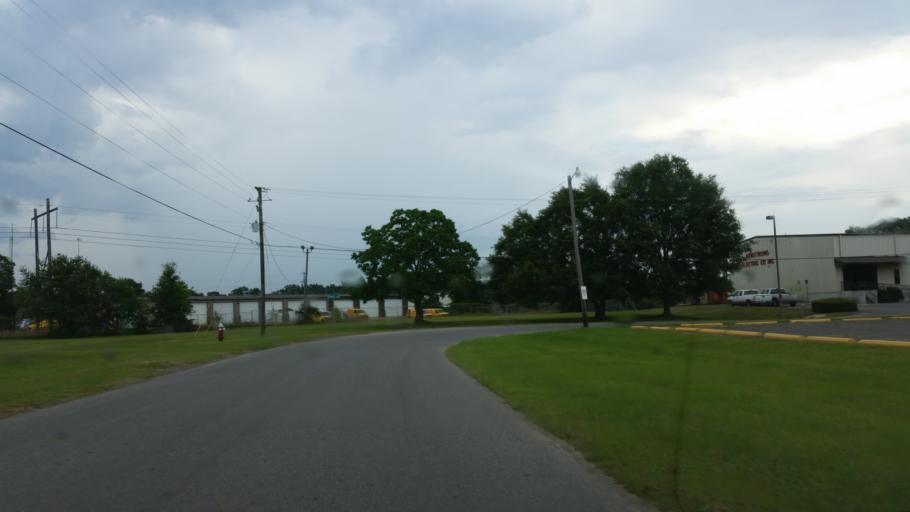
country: US
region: Florida
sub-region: Escambia County
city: Brent
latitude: 30.4669
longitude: -87.2315
